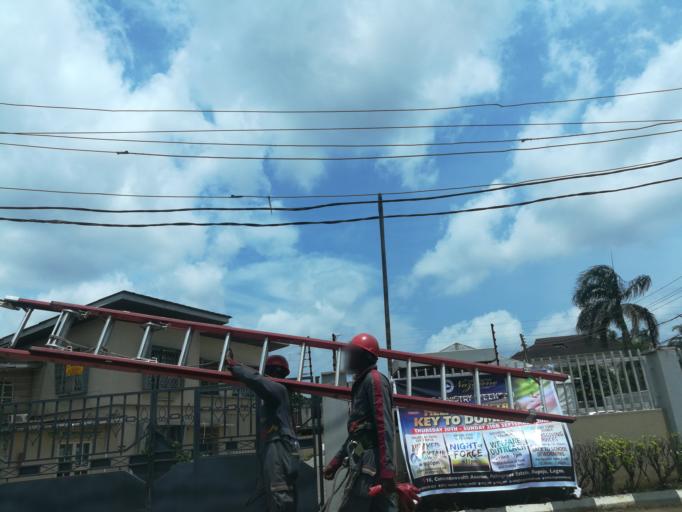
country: NG
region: Lagos
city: Somolu
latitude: 6.5431
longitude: 3.3625
